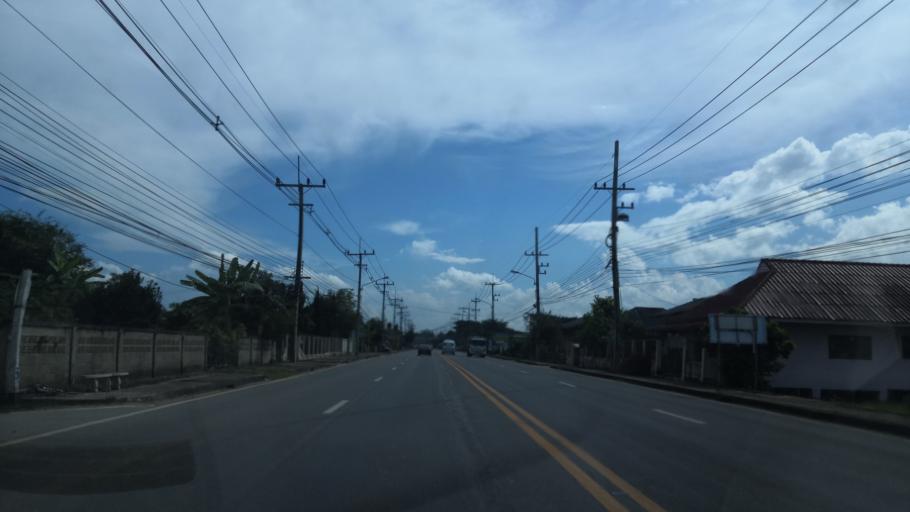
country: TH
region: Chiang Rai
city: Wiang Pa Pao
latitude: 19.2446
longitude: 99.5136
